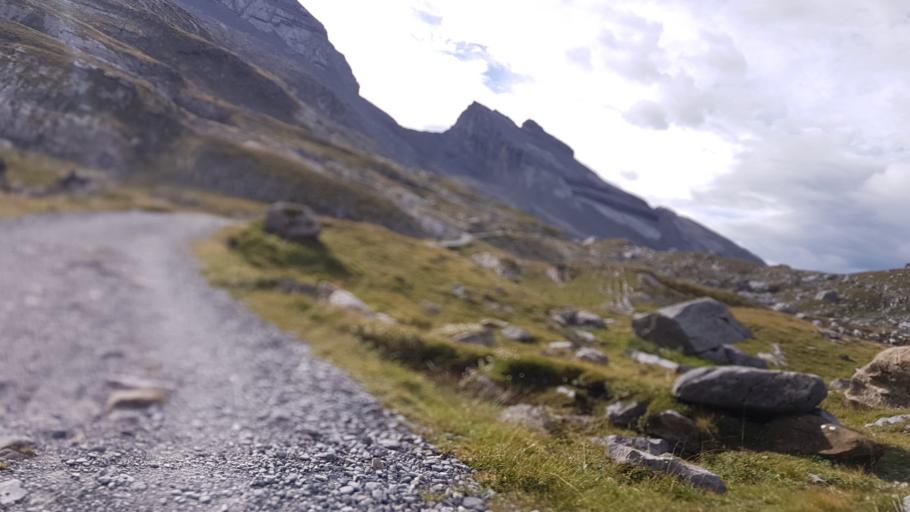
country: CH
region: Valais
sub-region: Leuk District
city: Leukerbad
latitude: 46.4231
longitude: 7.6225
